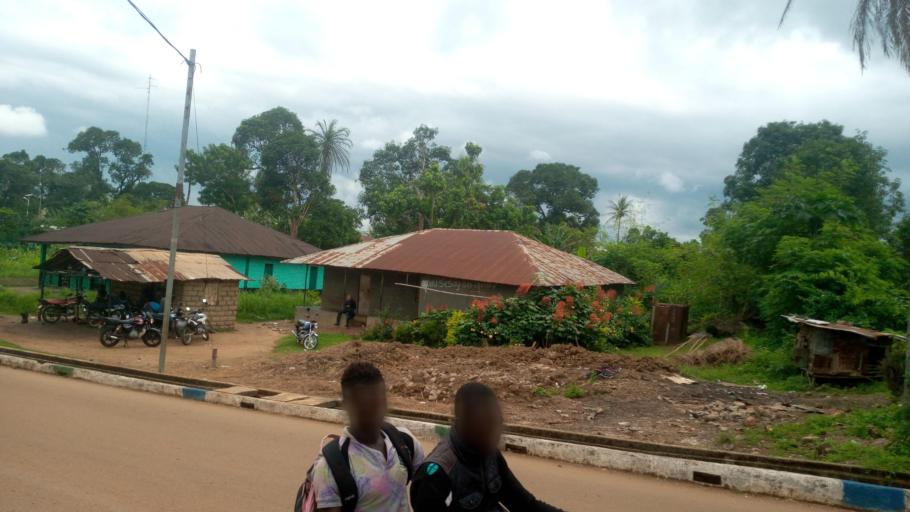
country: SL
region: Southern Province
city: Mogbwemo
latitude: 7.6055
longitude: -12.1742
